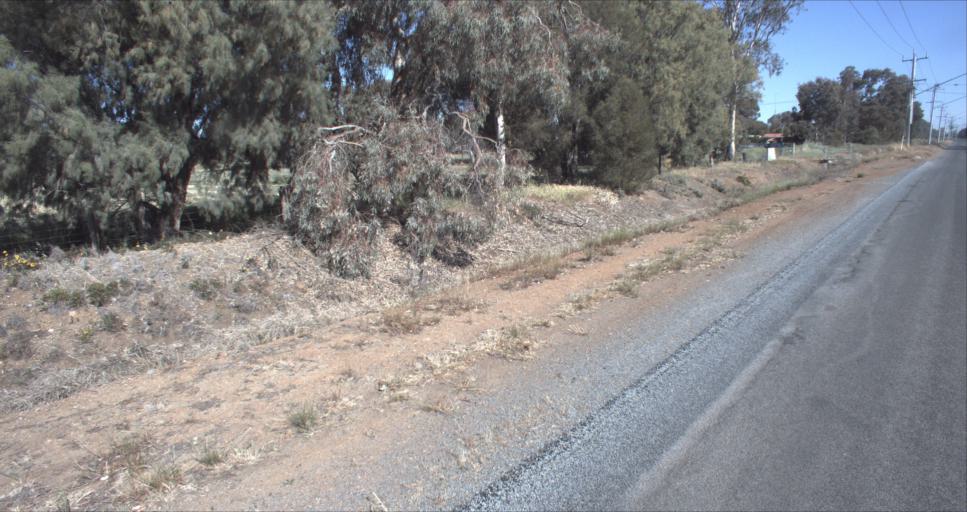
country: AU
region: New South Wales
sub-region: Leeton
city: Leeton
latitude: -34.5658
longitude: 146.4144
